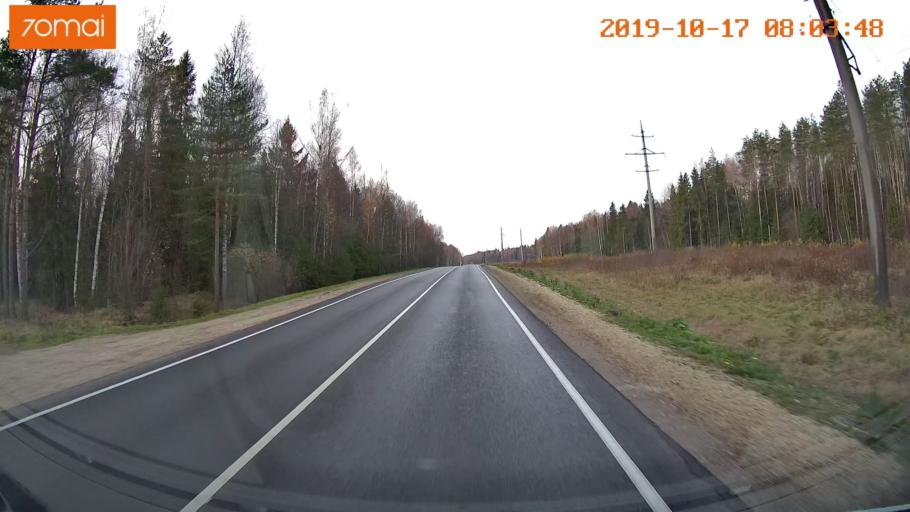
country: RU
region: Vladimir
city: Belaya Rechka
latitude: 56.3520
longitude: 39.4481
